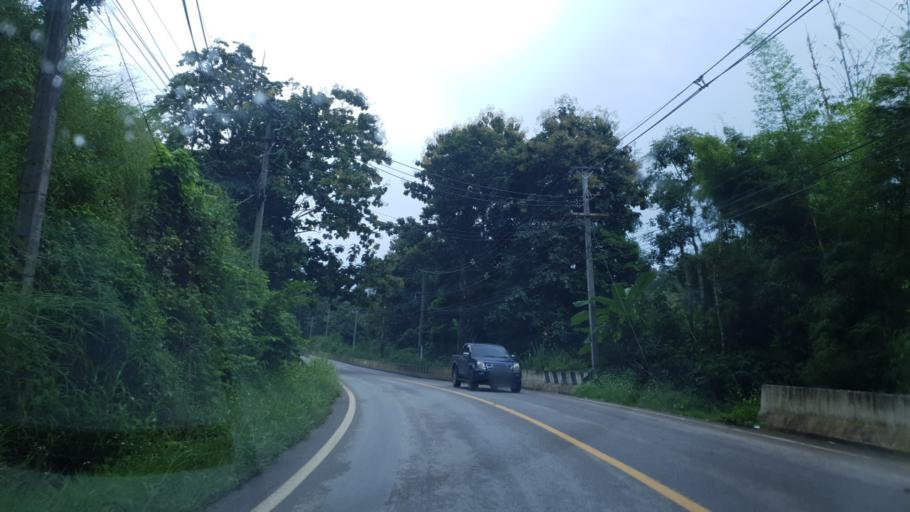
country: TH
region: Mae Hong Son
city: Ban Huai I Huak
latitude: 18.1368
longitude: 97.9952
